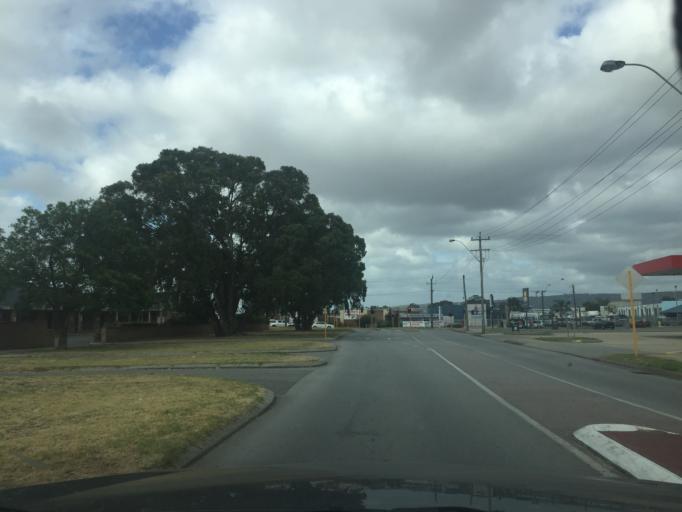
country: AU
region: Western Australia
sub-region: Gosnells
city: Maddington
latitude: -32.0494
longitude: 115.9769
